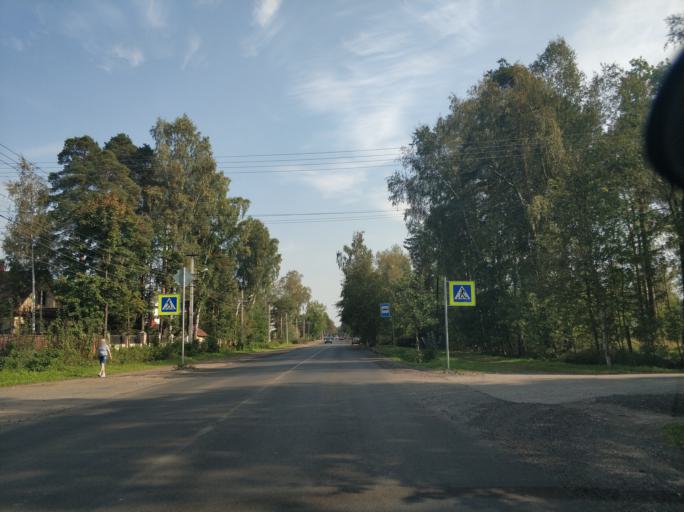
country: RU
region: Leningrad
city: Vsevolozhsk
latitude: 60.0187
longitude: 30.6394
